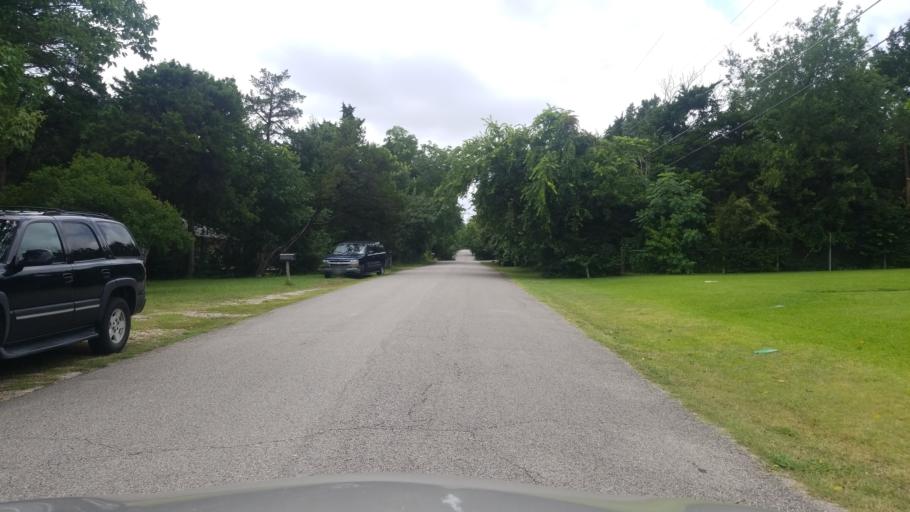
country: US
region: Texas
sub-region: Dallas County
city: Duncanville
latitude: 32.6798
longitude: -96.9295
